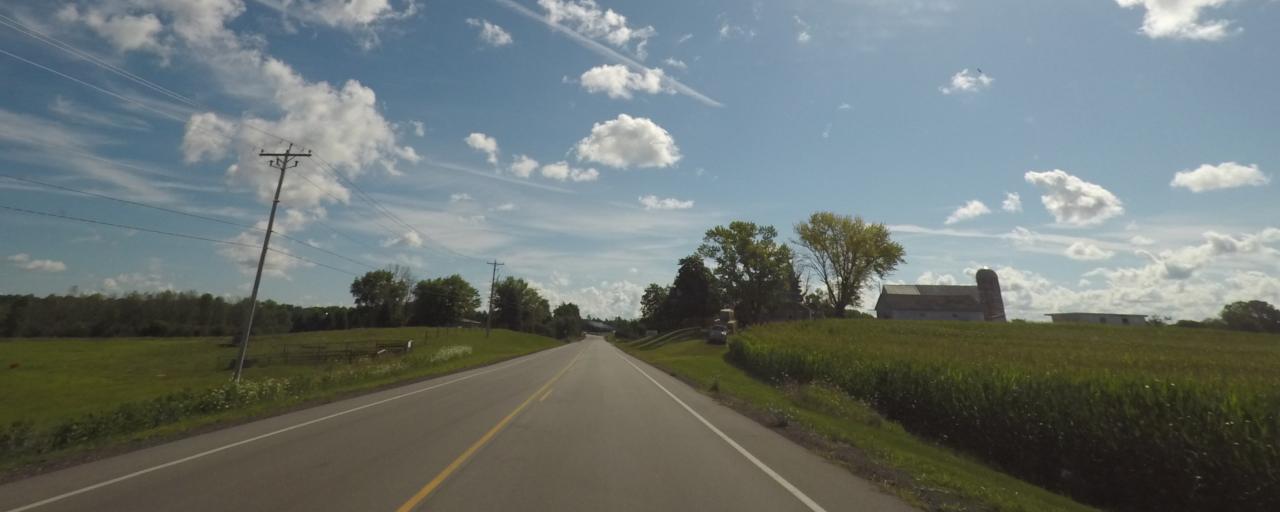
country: US
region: Wisconsin
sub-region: Waukesha County
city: Oconomowoc
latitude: 43.0753
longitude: -88.5497
